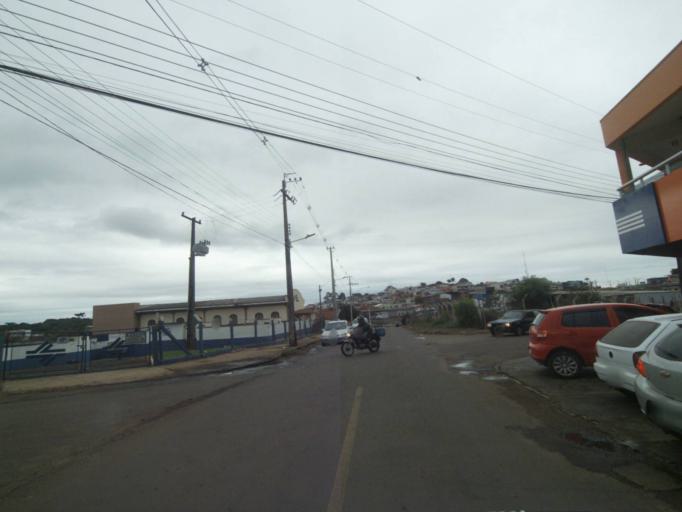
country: BR
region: Parana
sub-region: Telemaco Borba
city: Telemaco Borba
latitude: -24.3289
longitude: -50.6436
